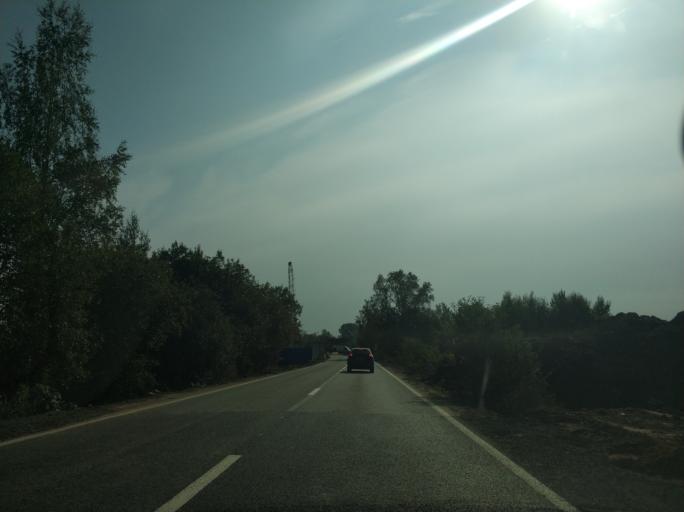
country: RU
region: St.-Petersburg
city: Krasnogvargeisky
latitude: 60.0085
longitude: 30.4854
